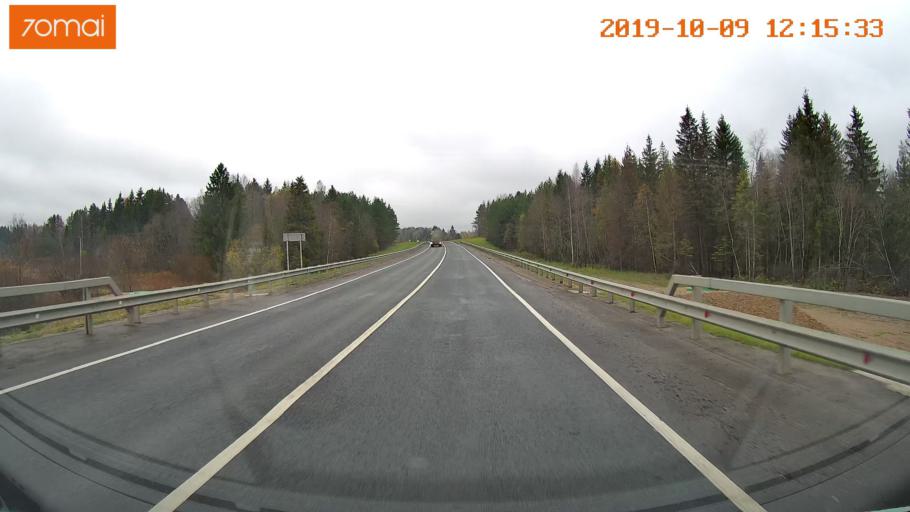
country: RU
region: Jaroslavl
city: Prechistoye
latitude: 58.4818
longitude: 40.3236
